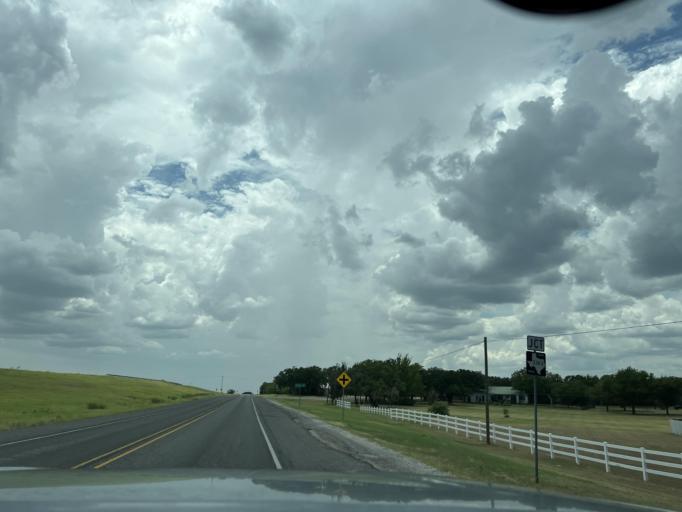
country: US
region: Texas
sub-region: Eastland County
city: Ranger
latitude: 32.4200
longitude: -98.7354
